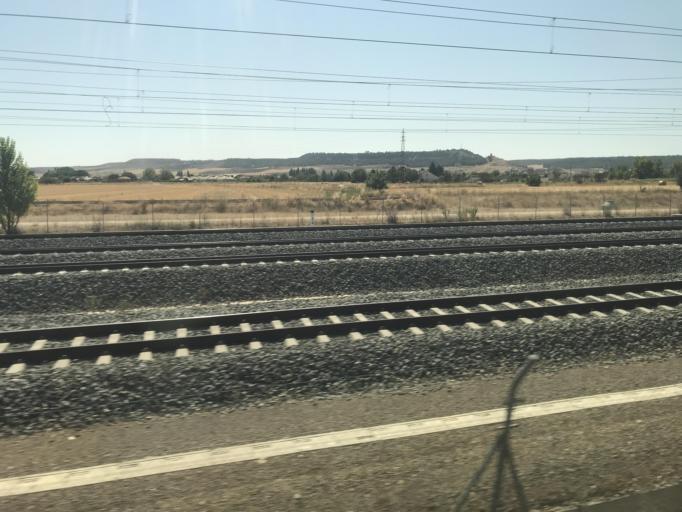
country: ES
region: Castille and Leon
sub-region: Provincia de Palencia
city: Venta de Banos
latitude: 41.9267
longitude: -4.4849
